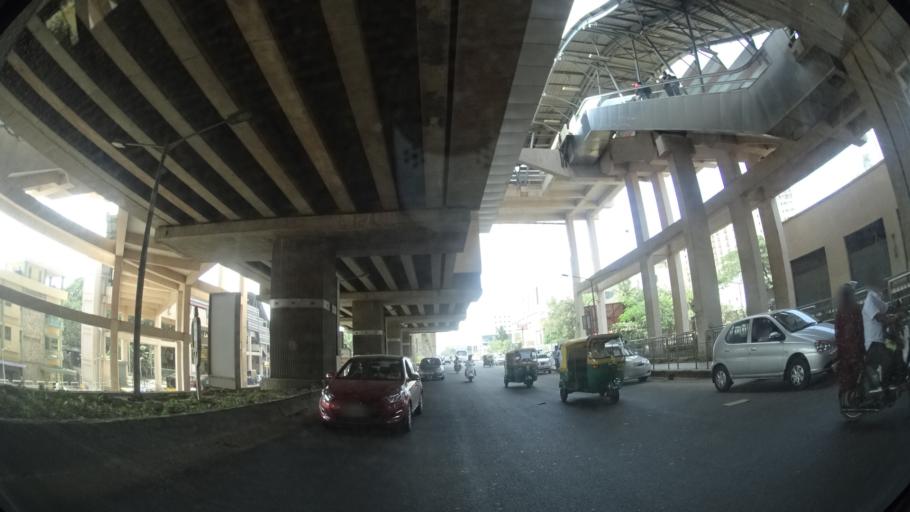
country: IN
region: Karnataka
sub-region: Bangalore Urban
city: Bangalore
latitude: 13.0239
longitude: 77.5500
